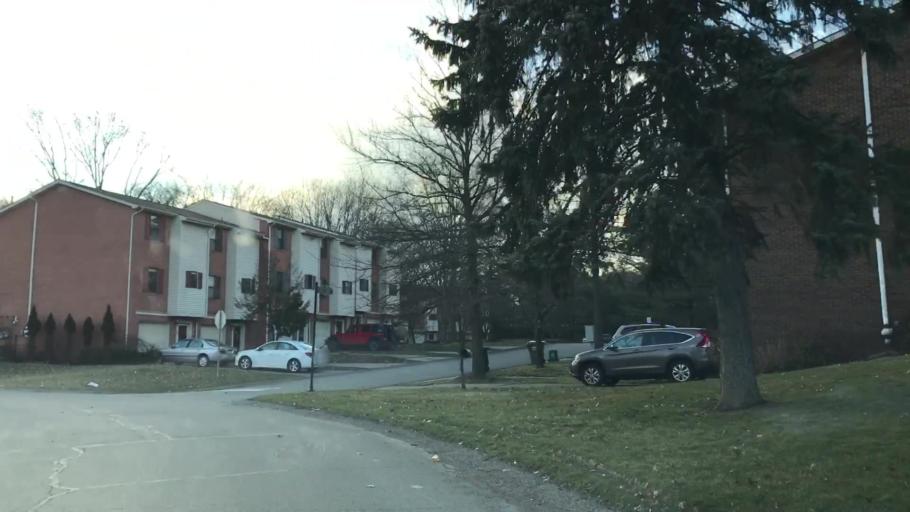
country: US
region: Pennsylvania
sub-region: Butler County
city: Seven Fields
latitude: 40.6857
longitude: -80.0598
